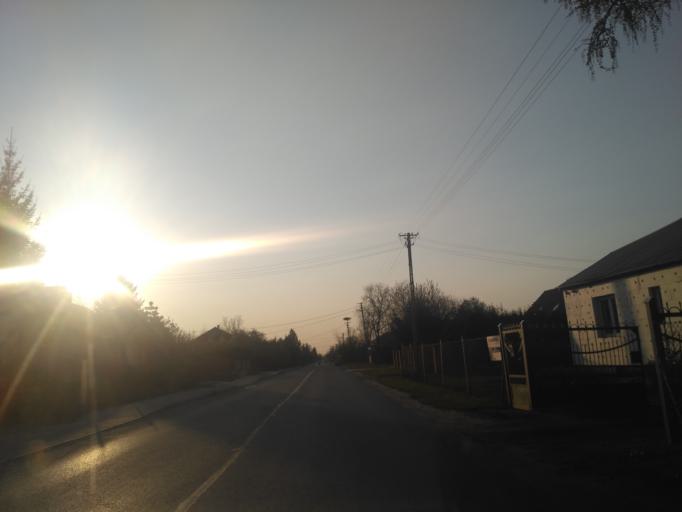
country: PL
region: Lublin Voivodeship
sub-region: Powiat chelmski
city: Pokrowka
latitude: 51.0891
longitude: 23.5101
